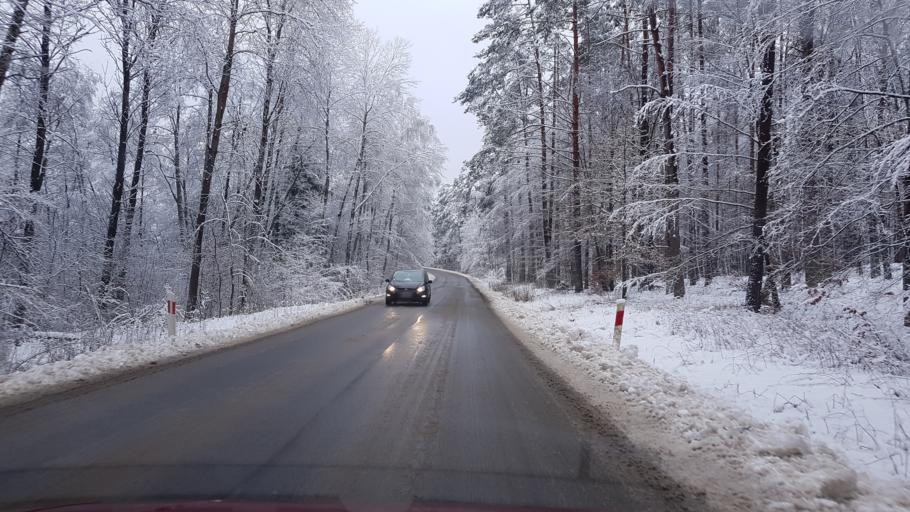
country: PL
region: West Pomeranian Voivodeship
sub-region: Powiat drawski
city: Zlocieniec
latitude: 53.5896
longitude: 16.0031
